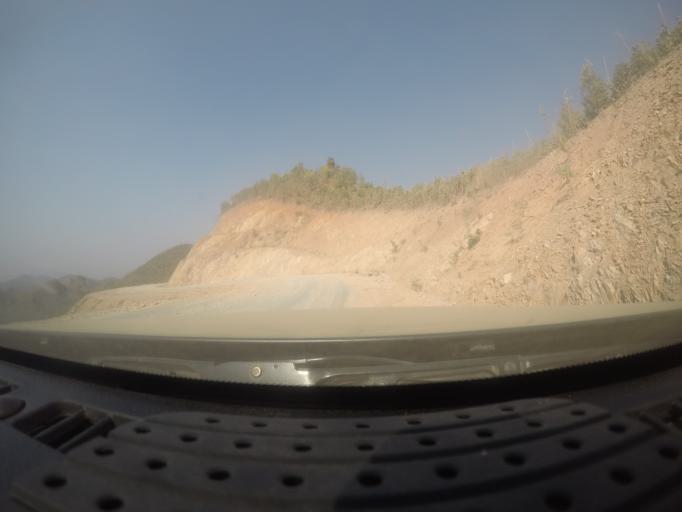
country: MM
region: Mandalay
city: Kyaukse
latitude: 21.3753
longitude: 96.3788
